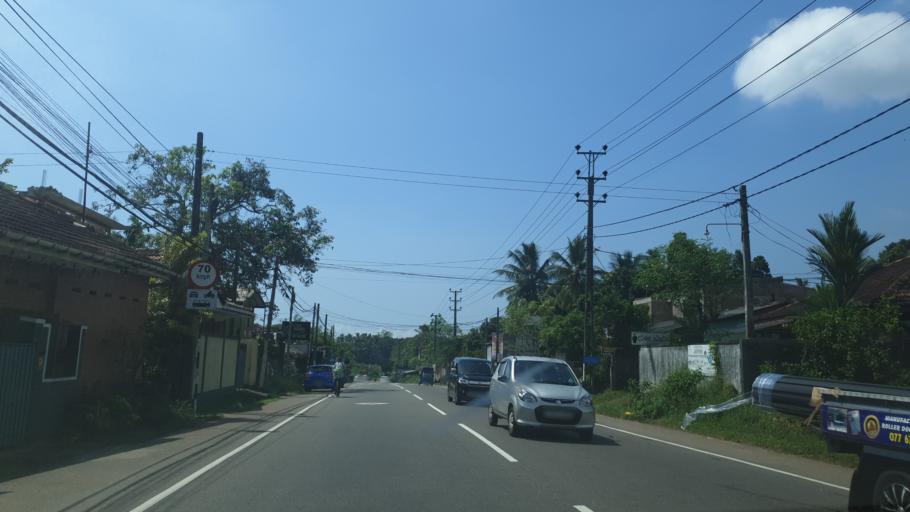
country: LK
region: Western
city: Panadura
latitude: 6.7098
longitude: 79.9813
